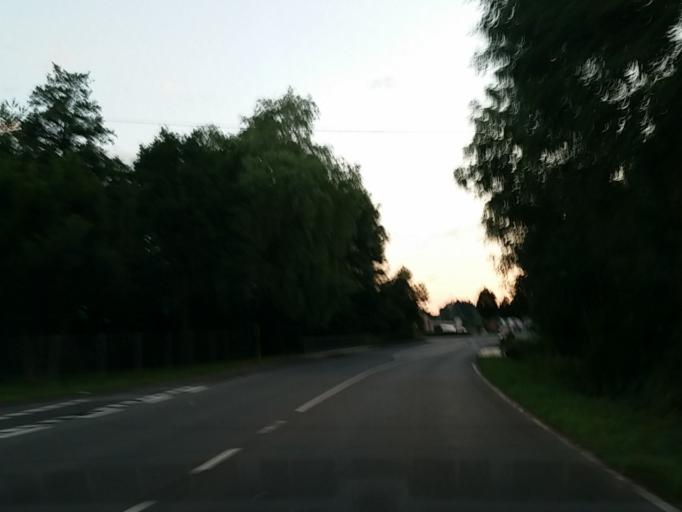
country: DE
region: Saarland
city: Wadern
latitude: 49.5279
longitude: 6.8978
